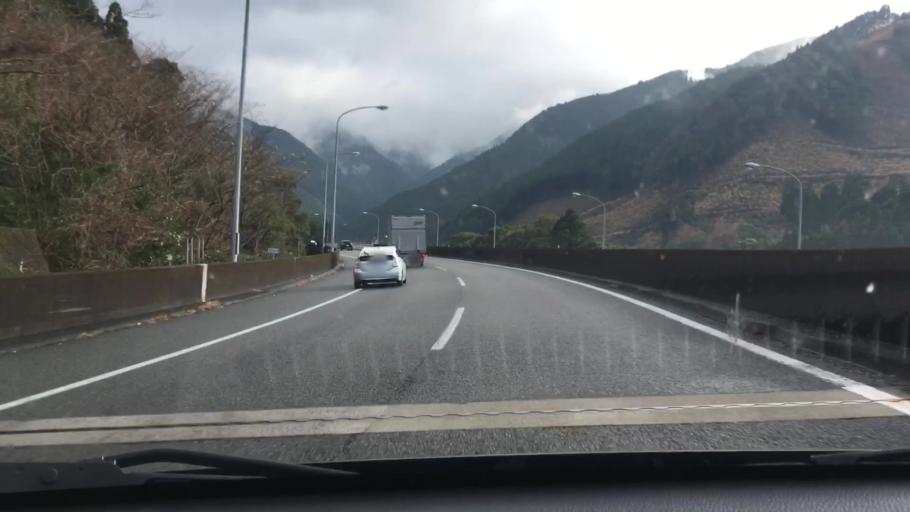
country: JP
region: Kumamoto
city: Yatsushiro
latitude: 32.4026
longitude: 130.6979
